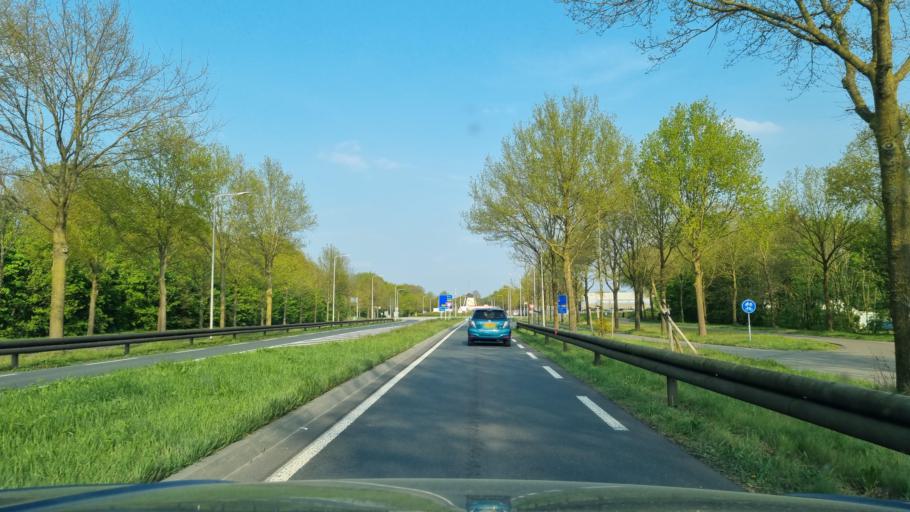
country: NL
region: North Brabant
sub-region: Gemeente Landerd
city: Reek
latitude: 51.7371
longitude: 5.6671
